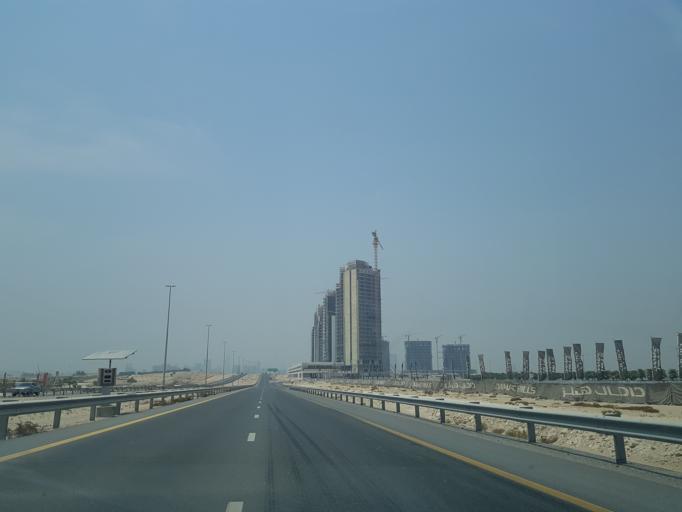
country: AE
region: Dubai
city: Dubai
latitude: 25.0147
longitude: 55.2487
